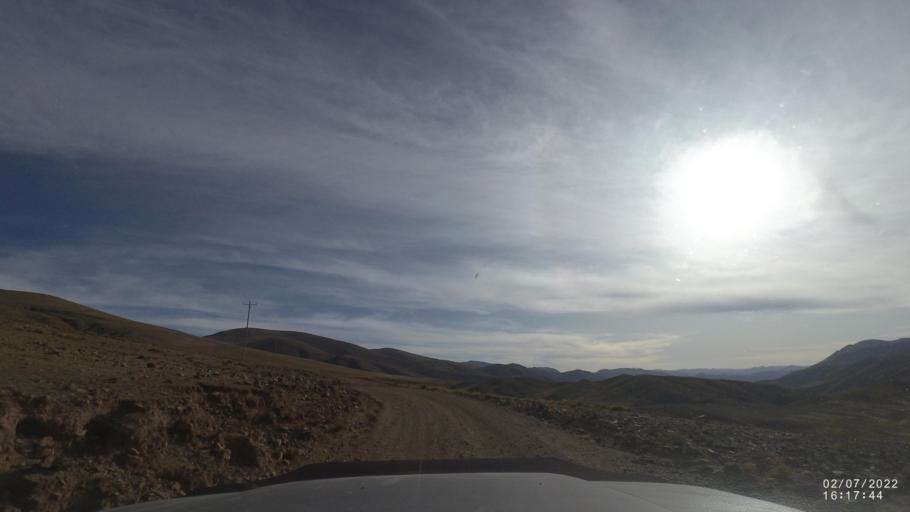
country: BO
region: Cochabamba
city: Irpa Irpa
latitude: -17.9247
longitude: -66.4395
